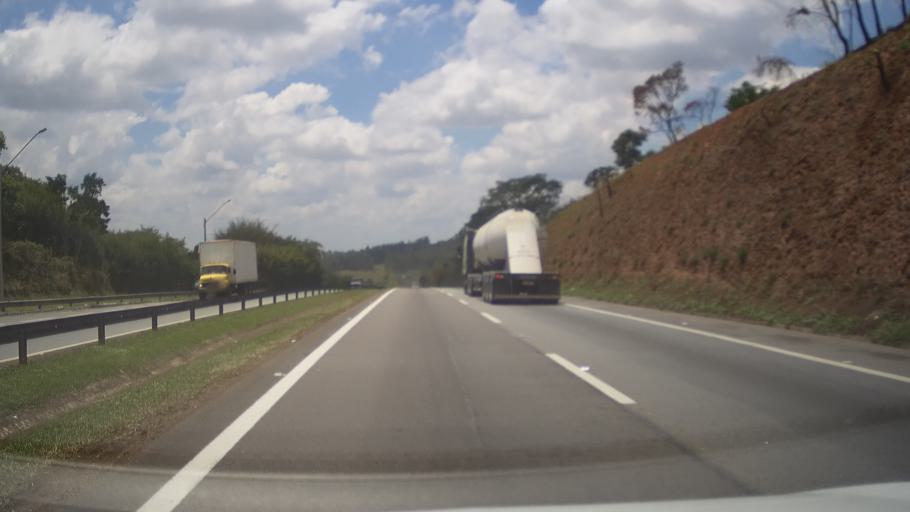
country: BR
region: Minas Gerais
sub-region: Tres Coracoes
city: Tres Coracoes
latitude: -21.6970
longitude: -45.3641
